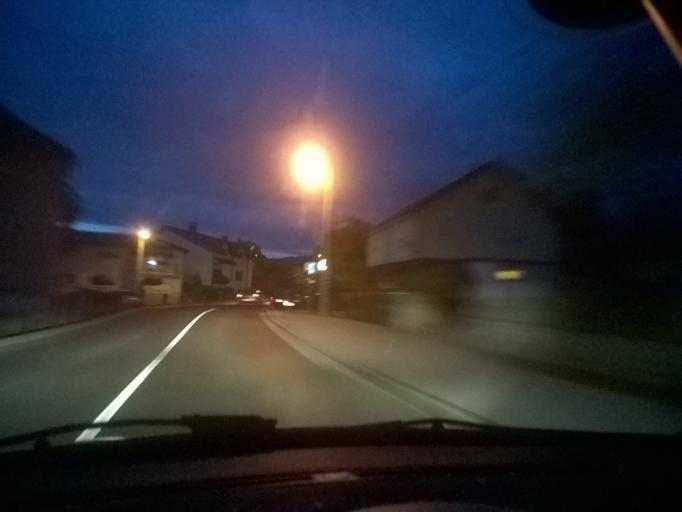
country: HR
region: Krapinsko-Zagorska
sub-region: Grad Krapina
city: Krapina
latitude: 46.1162
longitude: 15.8932
